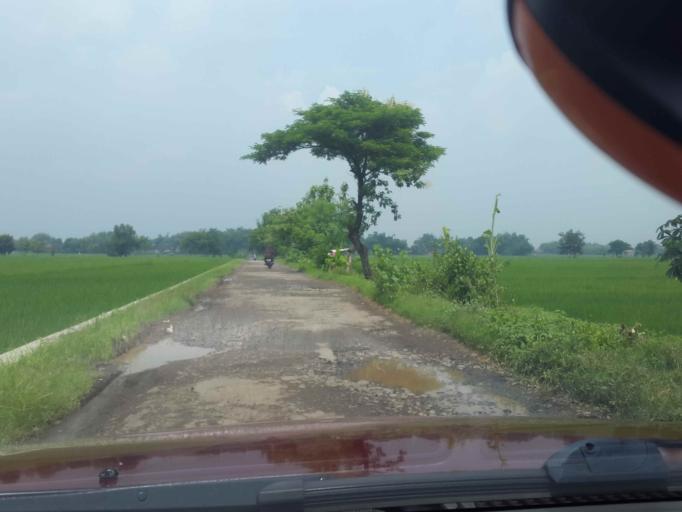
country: ID
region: Central Java
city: Jaten
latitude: -7.5624
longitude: 110.9391
